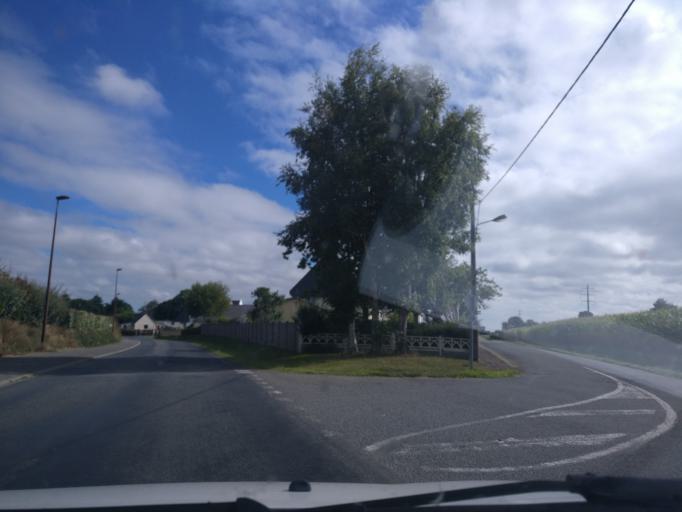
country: FR
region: Brittany
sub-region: Departement des Cotes-d'Armor
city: Rospez
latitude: 48.7271
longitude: -3.3873
